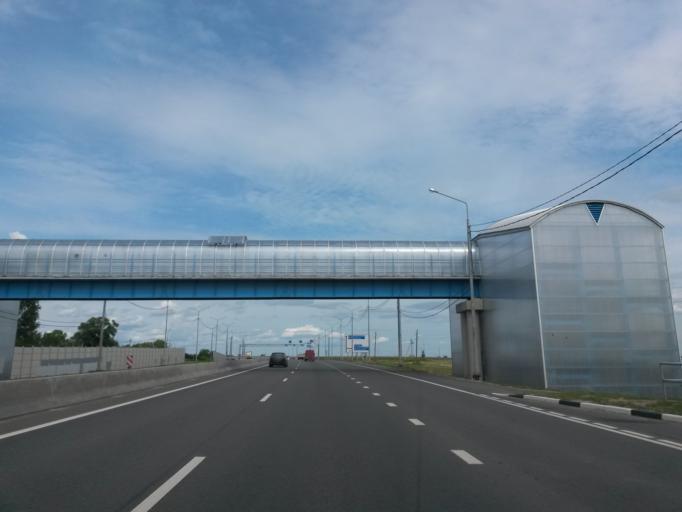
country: RU
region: Jaroslavl
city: Yaroslavl
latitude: 57.7177
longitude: 39.9029
